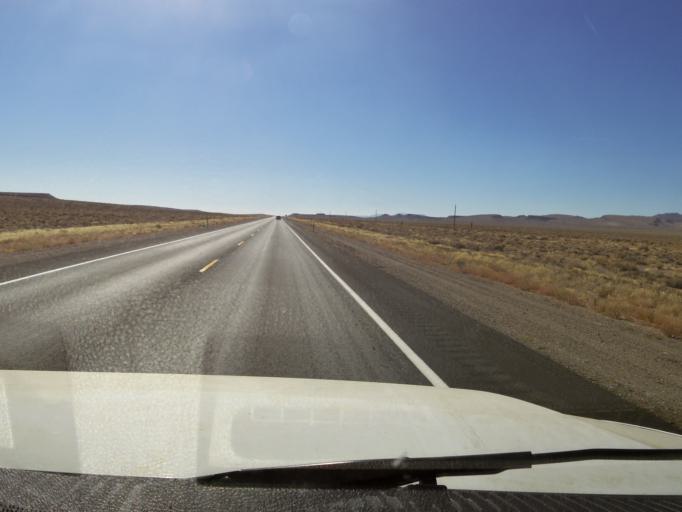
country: US
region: Nevada
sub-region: Esmeralda County
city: Goldfield
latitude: 37.4275
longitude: -117.1594
